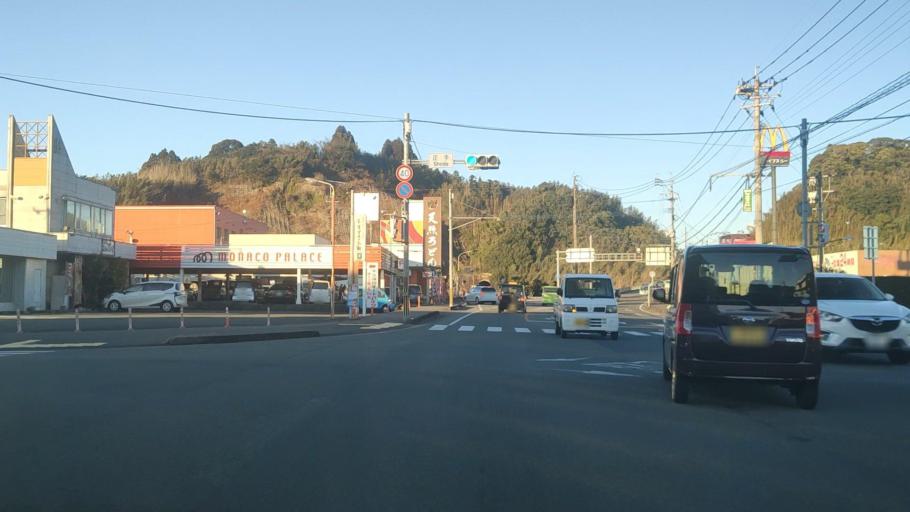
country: JP
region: Miyazaki
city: Miyazaki-shi
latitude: 31.8614
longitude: 131.3858
